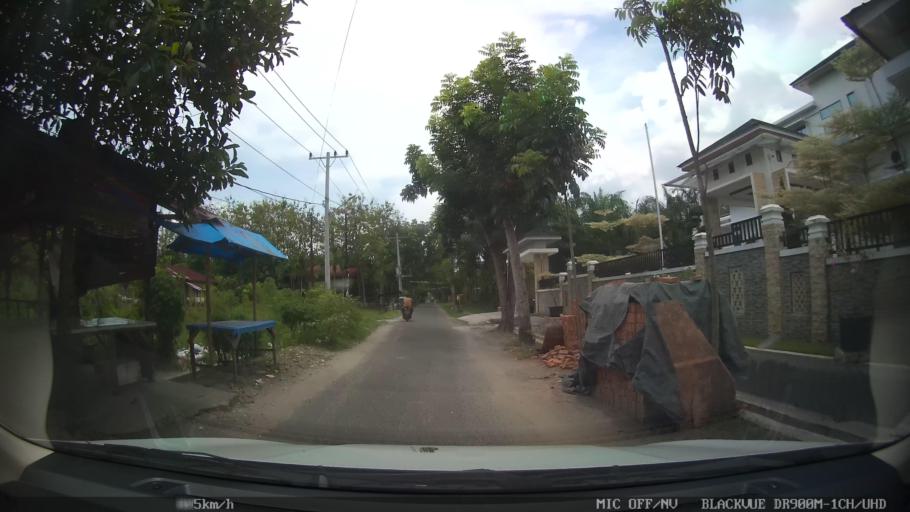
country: ID
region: North Sumatra
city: Binjai
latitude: 3.6209
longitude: 98.5097
